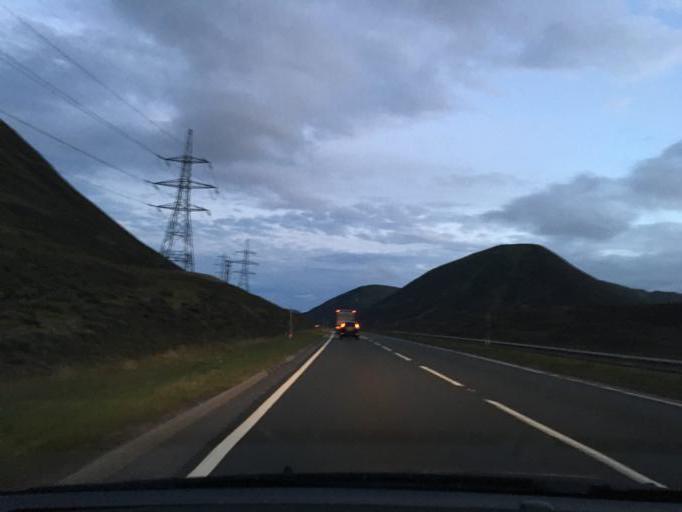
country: GB
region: Scotland
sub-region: Highland
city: Kingussie
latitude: 56.8730
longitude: -4.2570
